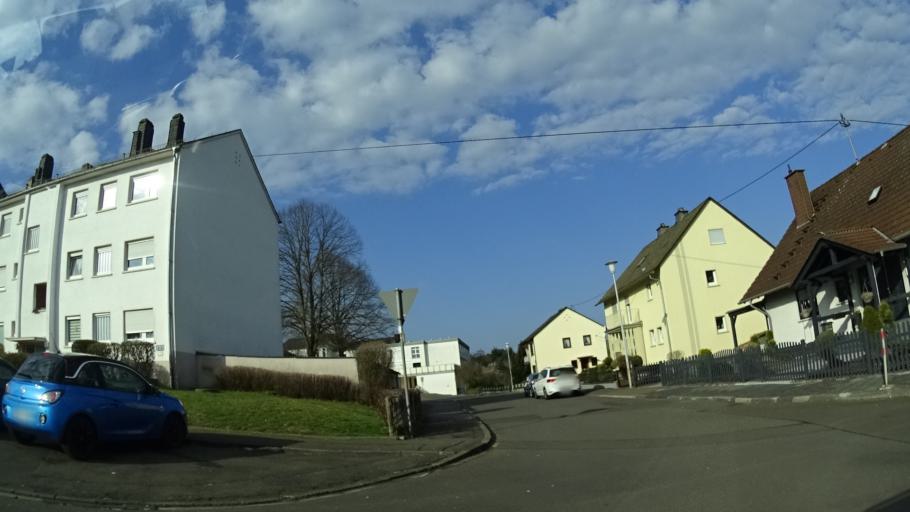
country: DE
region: Rheinland-Pfalz
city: Idar-Oberstein
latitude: 49.6967
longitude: 7.3275
